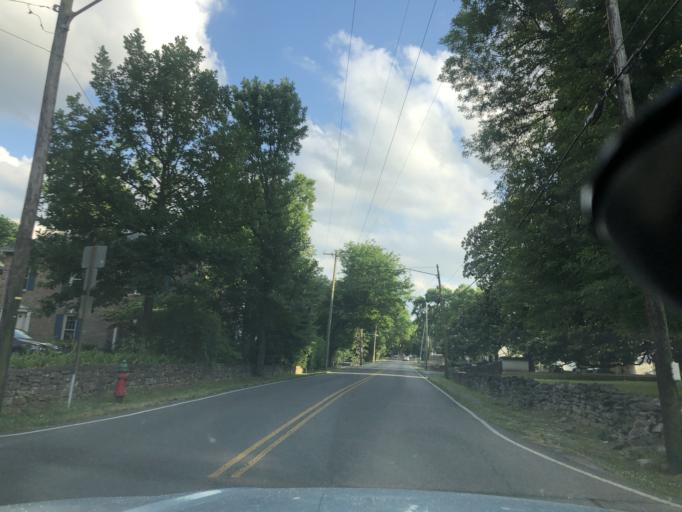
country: US
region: Tennessee
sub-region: Davidson County
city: Oak Hill
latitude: 36.1141
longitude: -86.7922
